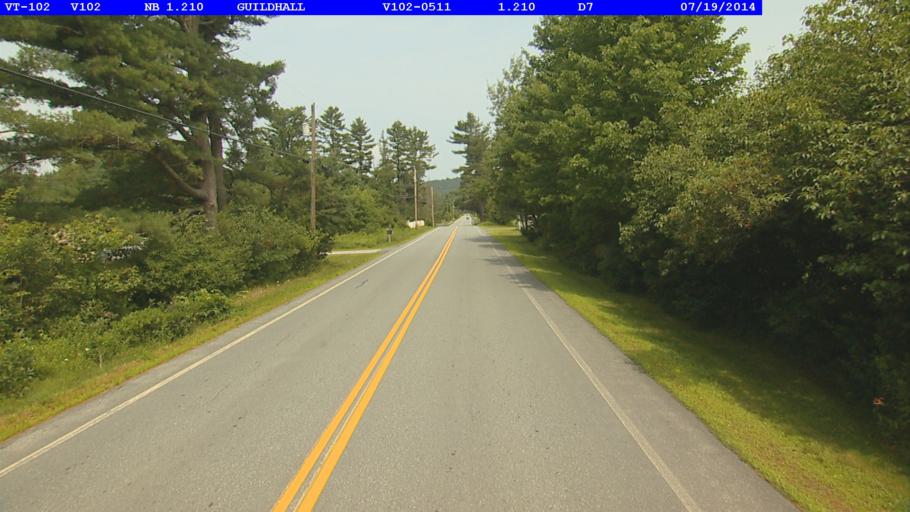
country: US
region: New Hampshire
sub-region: Coos County
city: Lancaster
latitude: 44.5128
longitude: -71.5941
